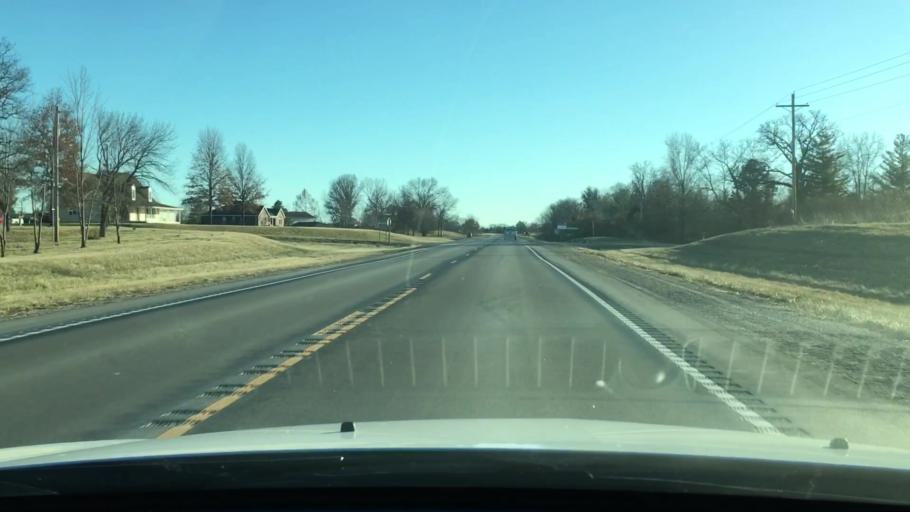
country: US
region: Missouri
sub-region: Boone County
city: Centralia
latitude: 39.1699
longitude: -92.1777
